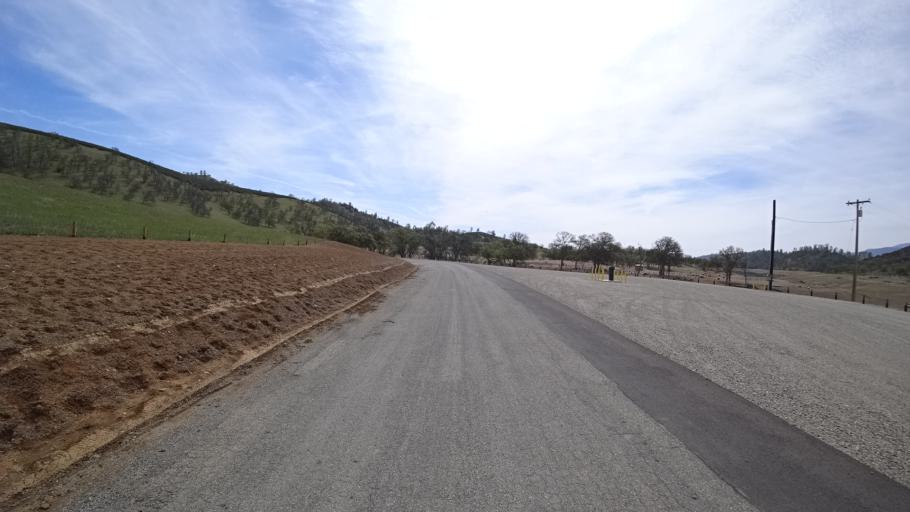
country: US
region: California
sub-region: Glenn County
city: Willows
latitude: 39.5947
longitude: -122.5268
